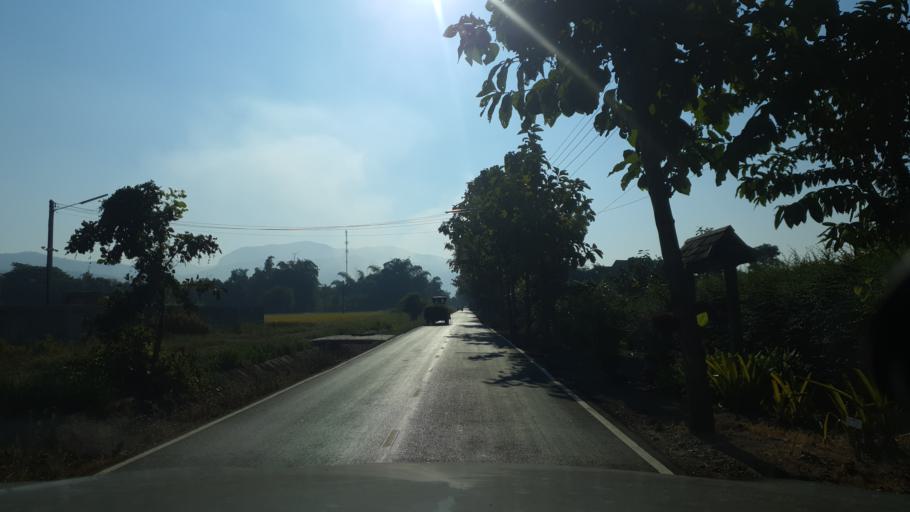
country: TH
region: Chiang Mai
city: San Kamphaeng
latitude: 18.6944
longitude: 99.1520
